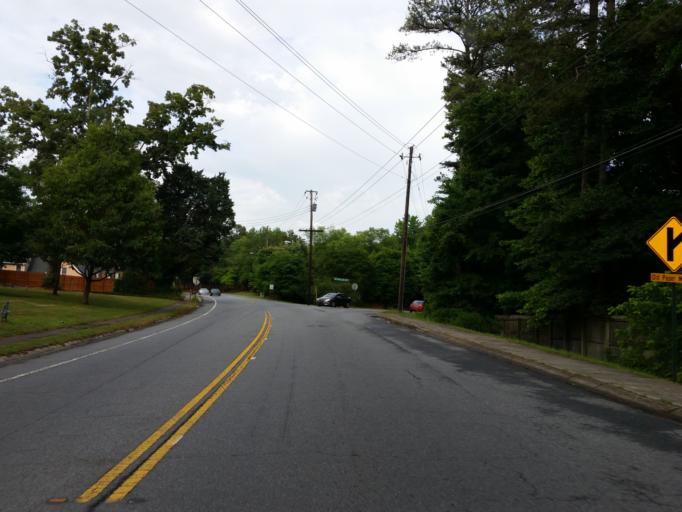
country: US
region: Georgia
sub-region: Cobb County
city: Smyrna
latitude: 33.9416
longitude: -84.4691
